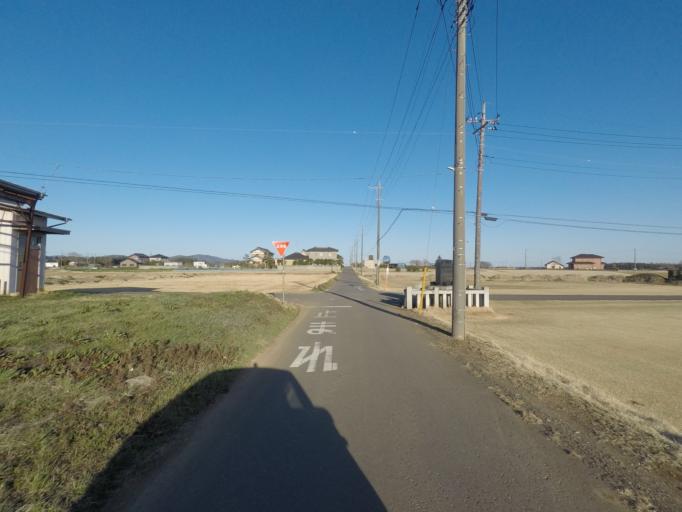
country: JP
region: Ibaraki
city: Ishige
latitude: 36.1344
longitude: 140.0134
